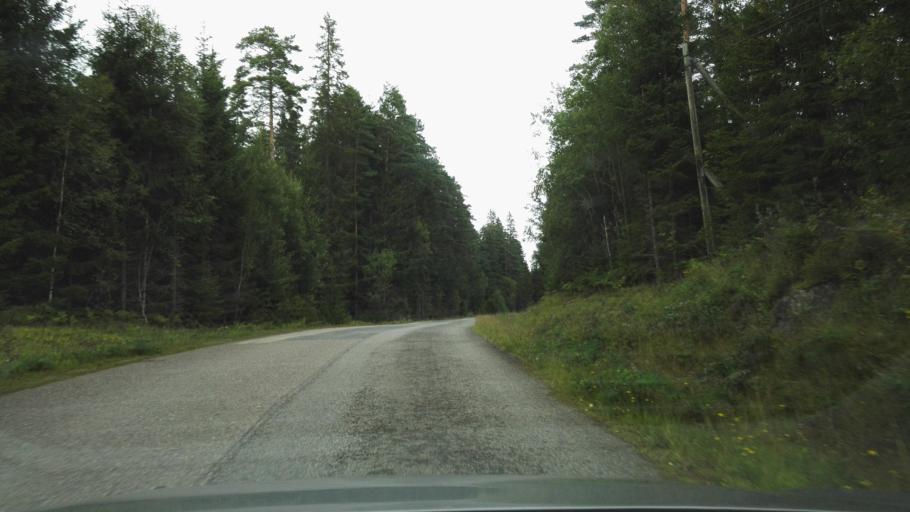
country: SE
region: Joenkoeping
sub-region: Vetlanda Kommun
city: Landsbro
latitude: 57.2984
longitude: 14.8520
